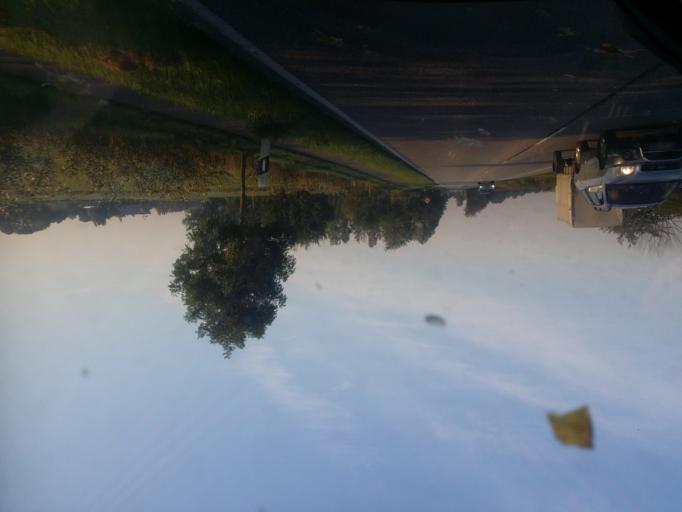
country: DE
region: Schleswig-Holstein
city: Hattstedtermarsch
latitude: 54.5455
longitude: 9.0087
